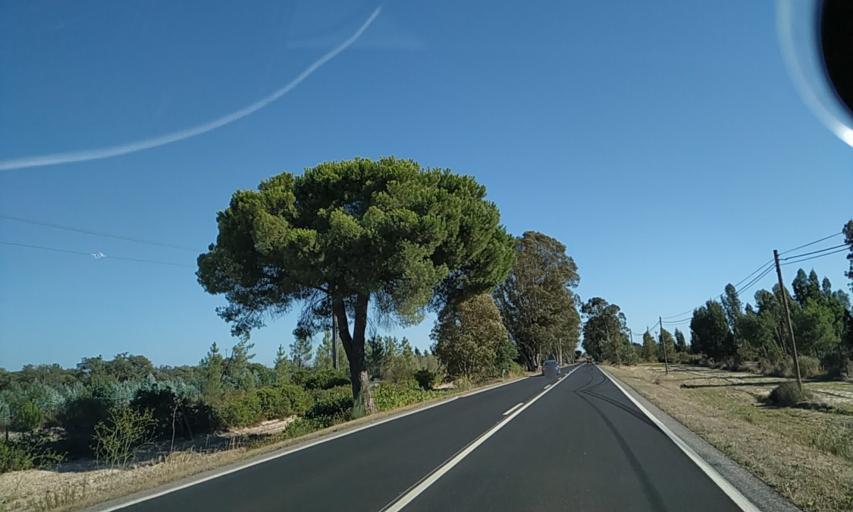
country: PT
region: Setubal
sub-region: Alcochete
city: Alcochete
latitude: 38.7917
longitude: -8.8807
